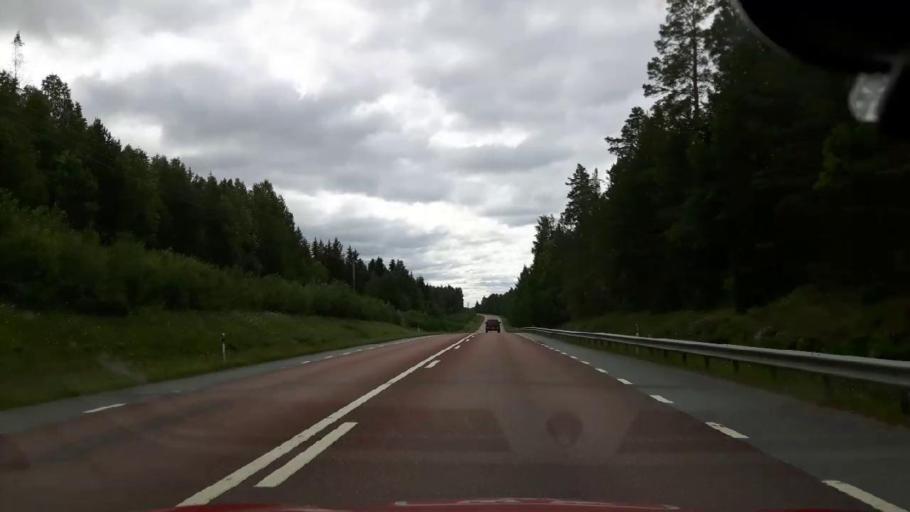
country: SE
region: Jaemtland
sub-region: Braecke Kommun
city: Braecke
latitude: 62.7981
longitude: 15.3723
